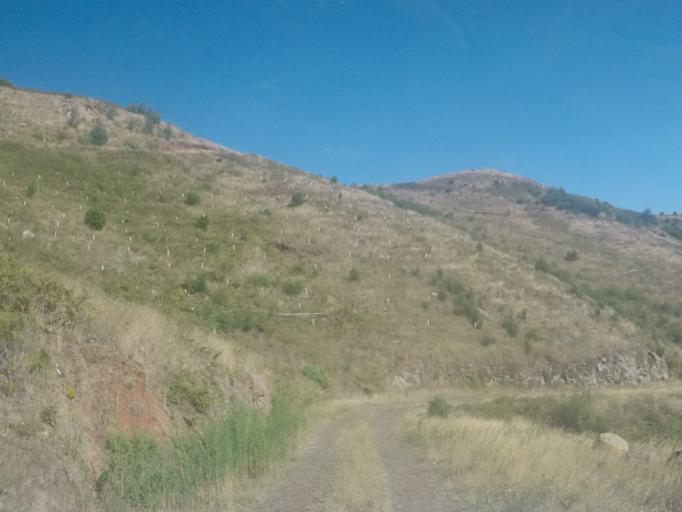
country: PT
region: Madeira
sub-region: Funchal
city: Nossa Senhora do Monte
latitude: 32.7020
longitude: -16.9165
